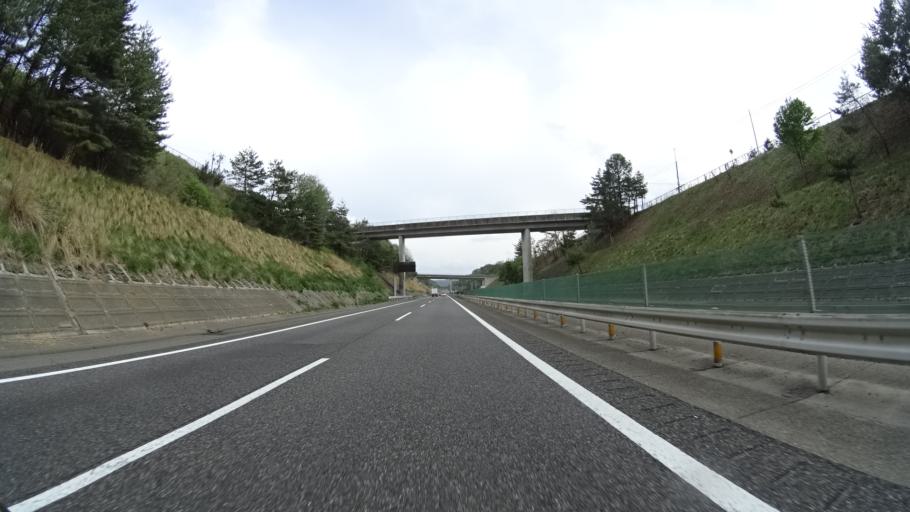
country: JP
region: Nagano
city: Shiojiri
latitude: 36.1226
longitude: 137.9788
